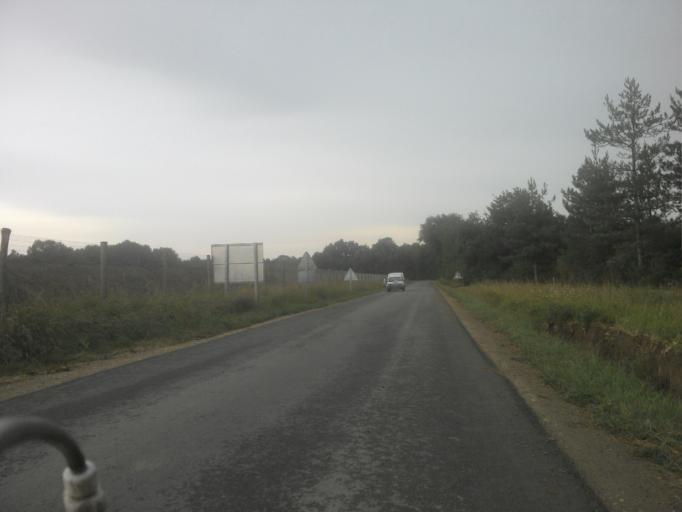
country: FR
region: Pays de la Loire
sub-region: Departement de Maine-et-Loire
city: Breze
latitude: 47.0946
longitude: -0.0012
